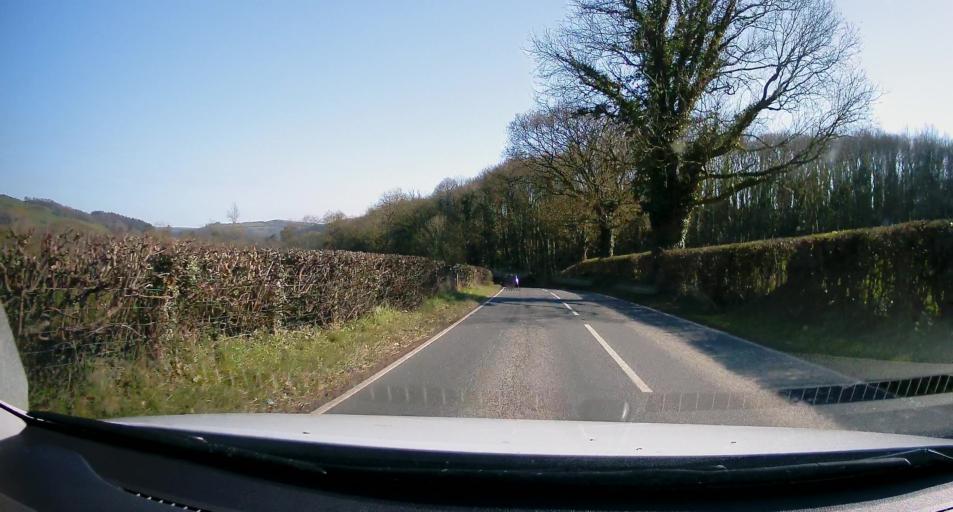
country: GB
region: Wales
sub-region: County of Ceredigion
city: Penparcau
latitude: 52.3671
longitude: -4.0652
